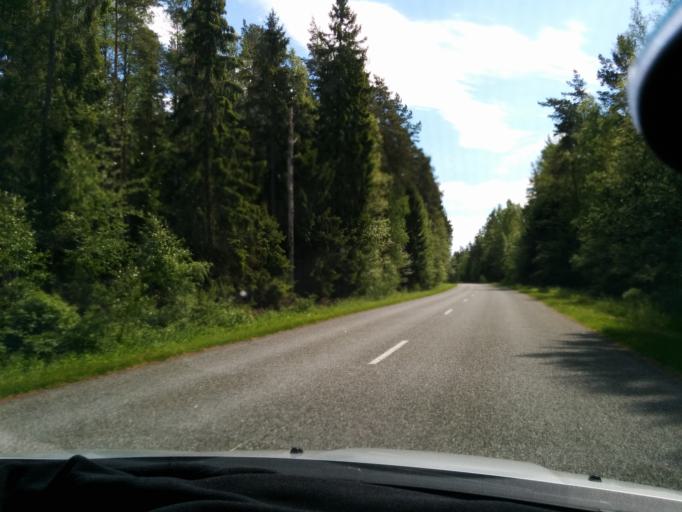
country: EE
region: Harju
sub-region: Loksa linn
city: Loksa
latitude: 59.5720
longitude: 25.9323
